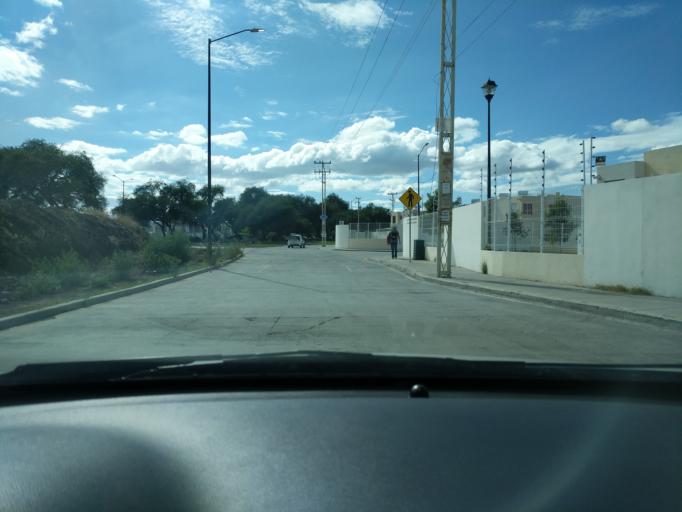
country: MX
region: Queretaro
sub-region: El Marques
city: General Lazaro Cardenas (El Colorado)
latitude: 20.5836
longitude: -100.2535
